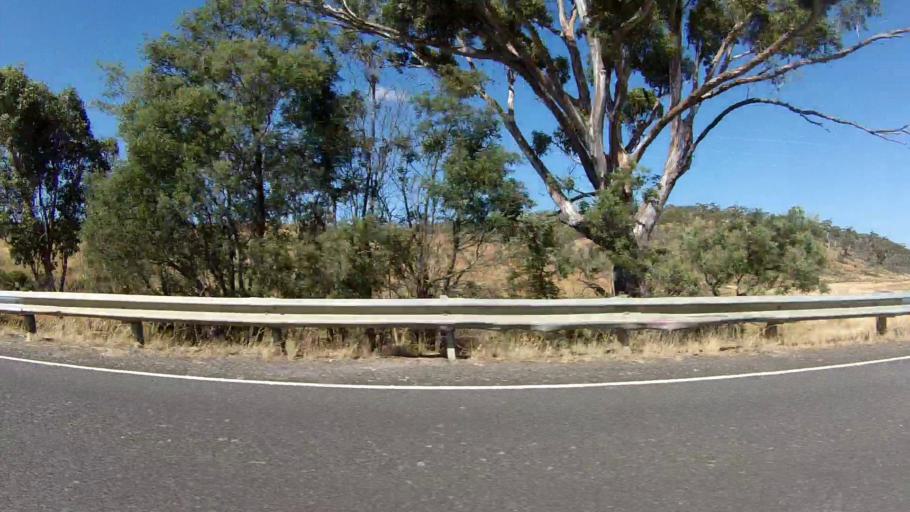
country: AU
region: Tasmania
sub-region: Sorell
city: Sorell
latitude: -42.5954
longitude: 147.7870
